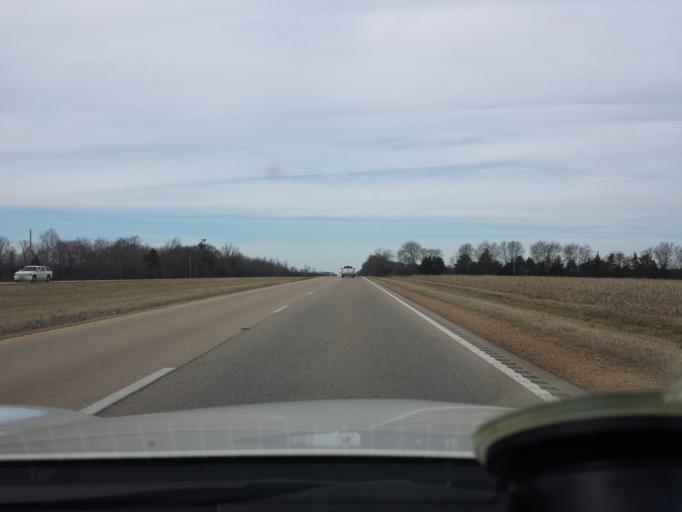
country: US
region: Mississippi
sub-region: Monroe County
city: Aberdeen
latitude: 33.8091
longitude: -88.7011
